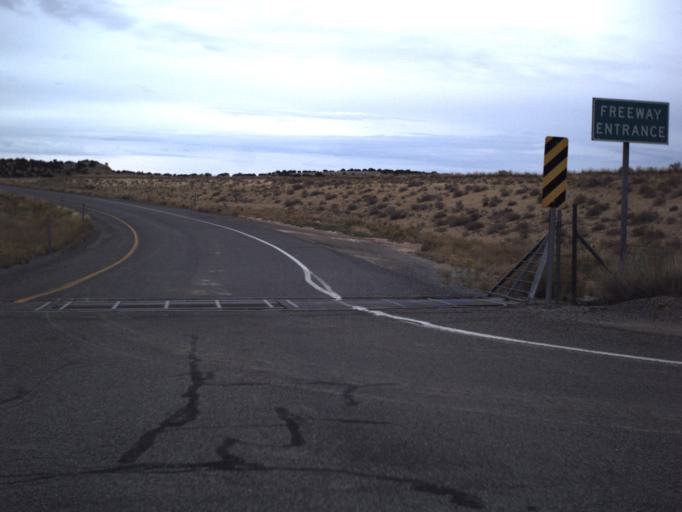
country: US
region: Utah
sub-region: Emery County
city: Castle Dale
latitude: 38.8804
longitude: -110.6582
